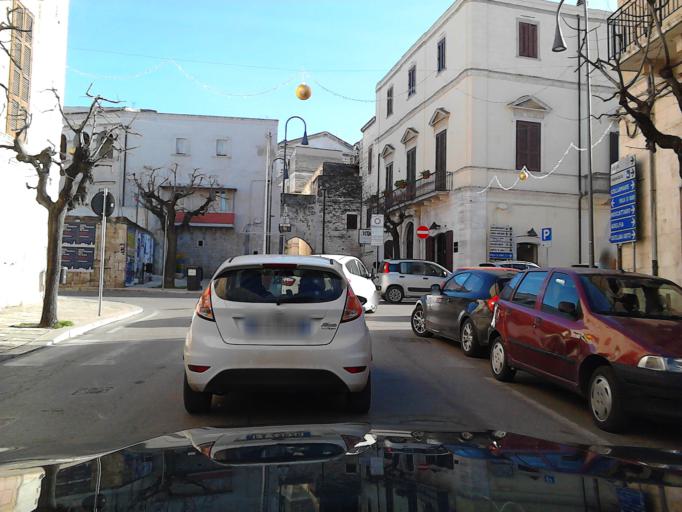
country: IT
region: Apulia
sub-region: Provincia di Bari
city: Rutigliano
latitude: 41.0115
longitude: 17.0036
